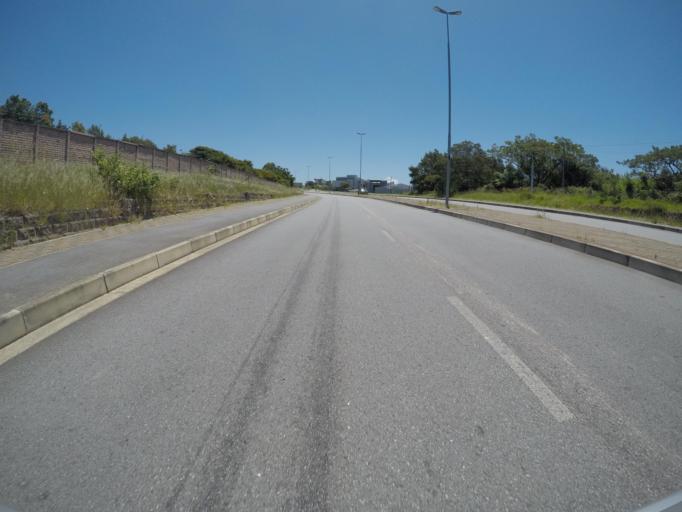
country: ZA
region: Eastern Cape
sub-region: Buffalo City Metropolitan Municipality
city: East London
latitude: -32.9509
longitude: 27.9468
